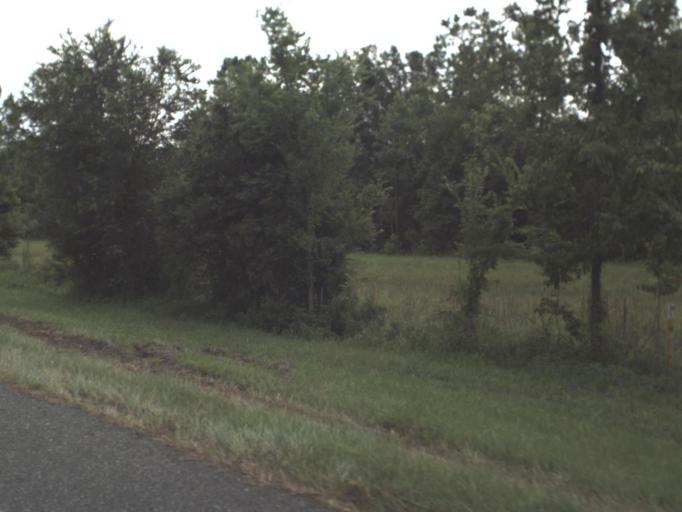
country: US
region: Florida
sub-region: Levy County
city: Bronson
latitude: 29.2870
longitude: -82.7437
